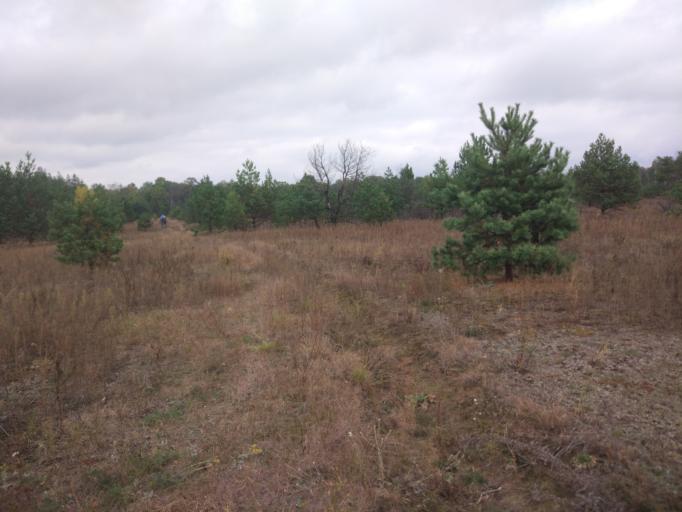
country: RU
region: Brjansk
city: Vyshkov
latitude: 52.5253
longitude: 31.5661
